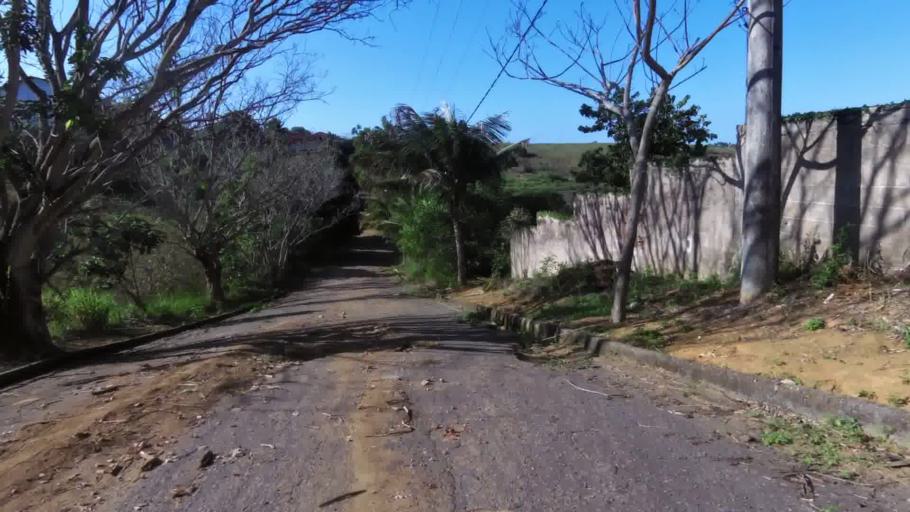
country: BR
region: Espirito Santo
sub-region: Guarapari
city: Guarapari
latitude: -20.7408
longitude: -40.5573
